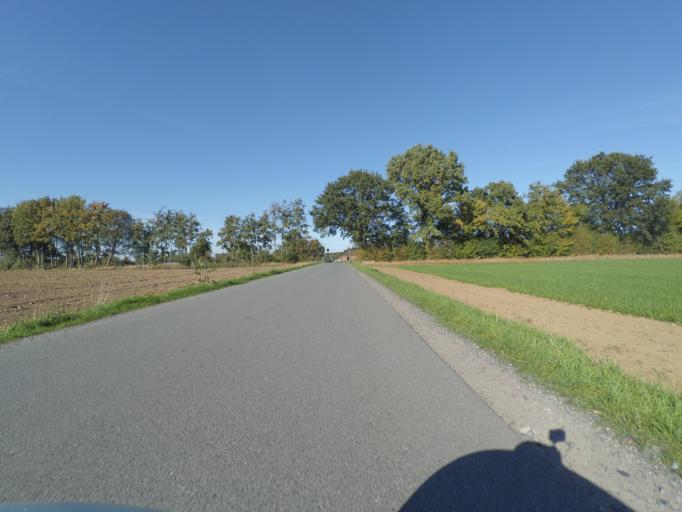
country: DE
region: North Rhine-Westphalia
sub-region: Regierungsbezirk Dusseldorf
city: Bocholt
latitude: 51.8542
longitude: 6.5666
